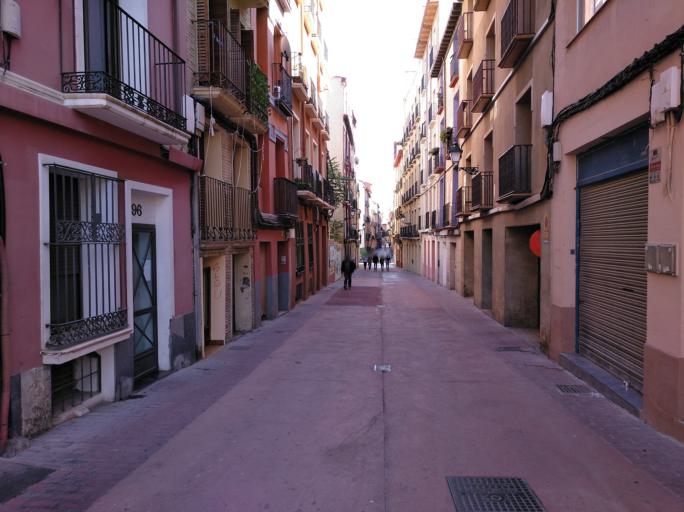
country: ES
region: Aragon
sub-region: Provincia de Zaragoza
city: Zaragoza
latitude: 41.6542
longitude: -0.8894
